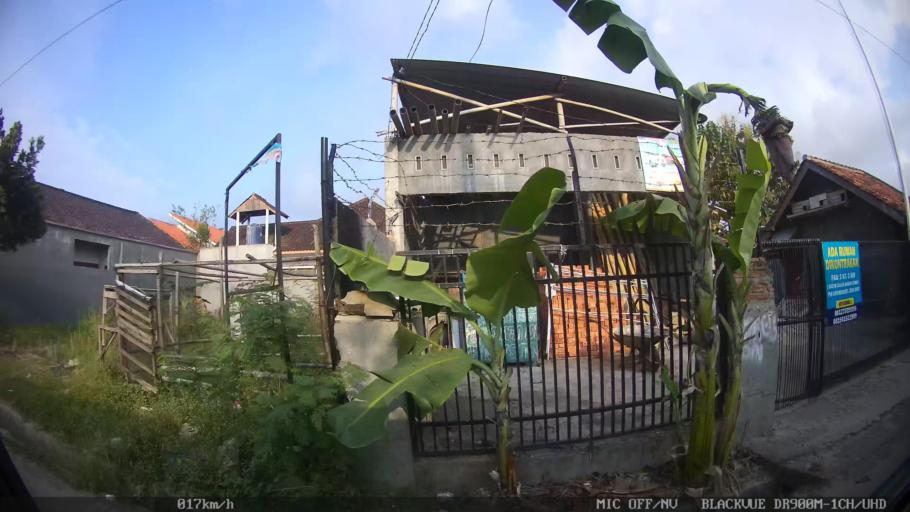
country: ID
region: Lampung
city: Kedaton
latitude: -5.4015
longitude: 105.3084
